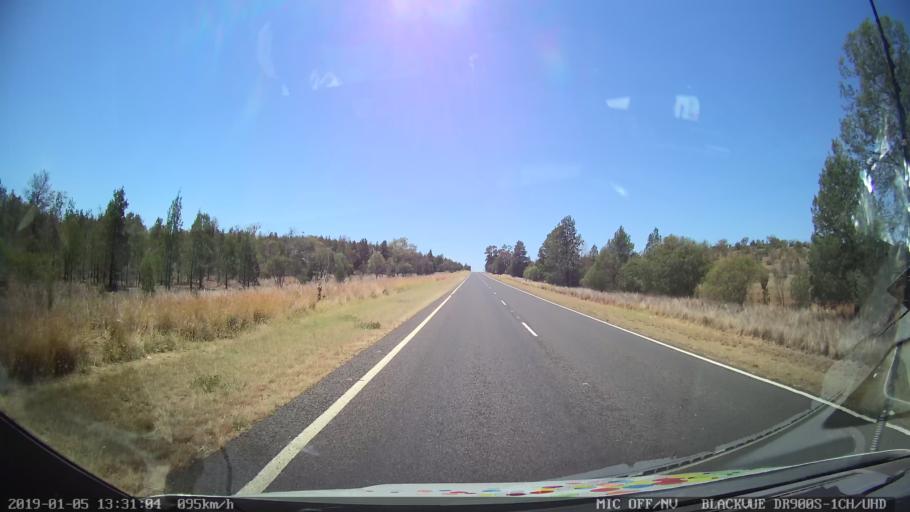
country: AU
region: New South Wales
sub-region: Gunnedah
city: Gunnedah
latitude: -31.0136
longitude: 150.0792
